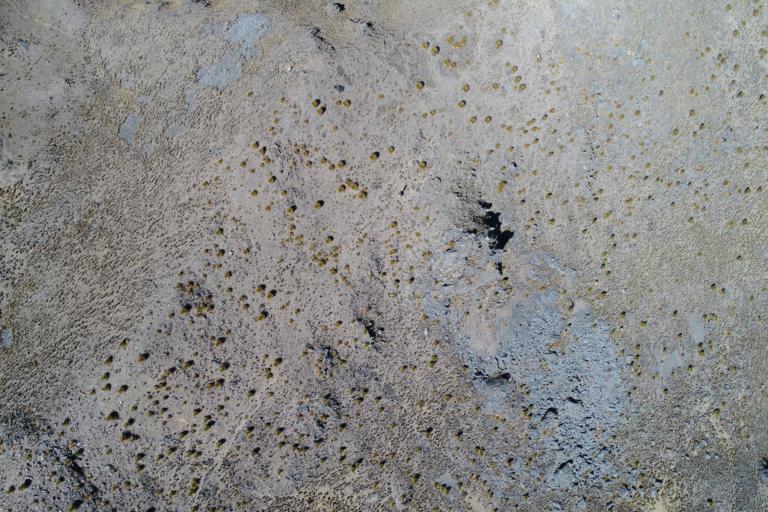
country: BO
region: La Paz
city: Viloco
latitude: -16.8105
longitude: -67.5446
